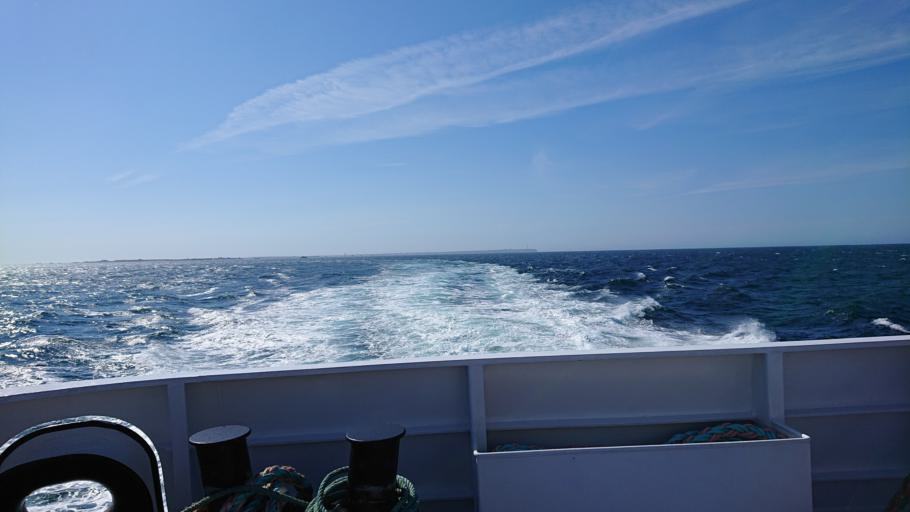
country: FR
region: Brittany
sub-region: Departement du Finistere
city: Le Conquet
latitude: 48.4135
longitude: -4.9373
